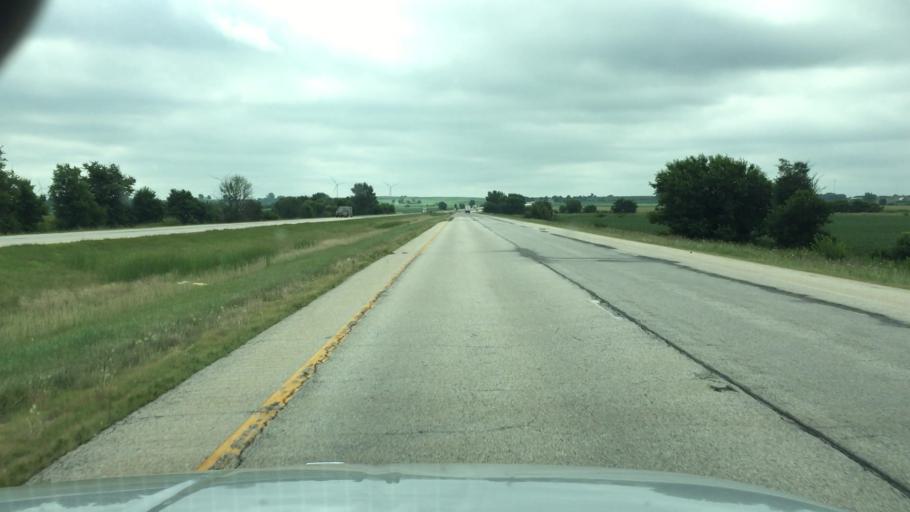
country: US
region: Illinois
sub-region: Henry County
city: Orion
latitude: 41.2704
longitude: -90.3319
